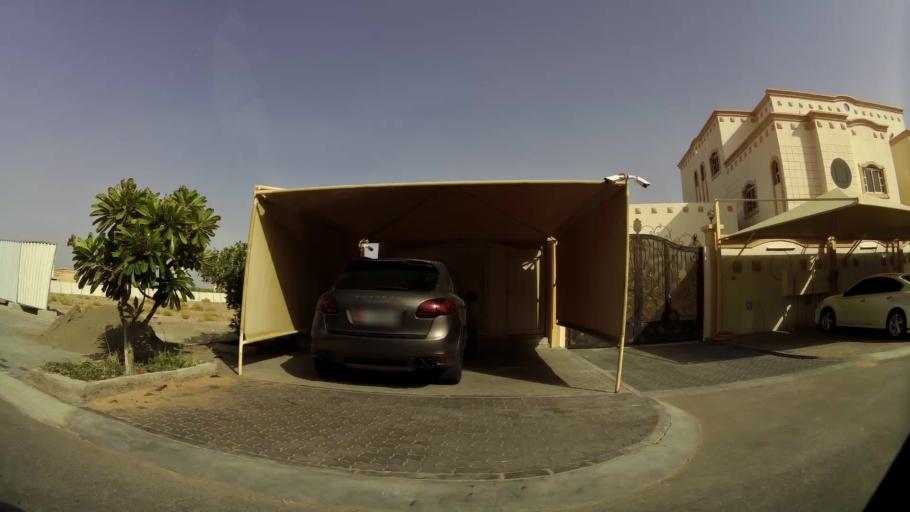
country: AE
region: Abu Dhabi
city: Al Ain
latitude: 24.2244
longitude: 55.6506
